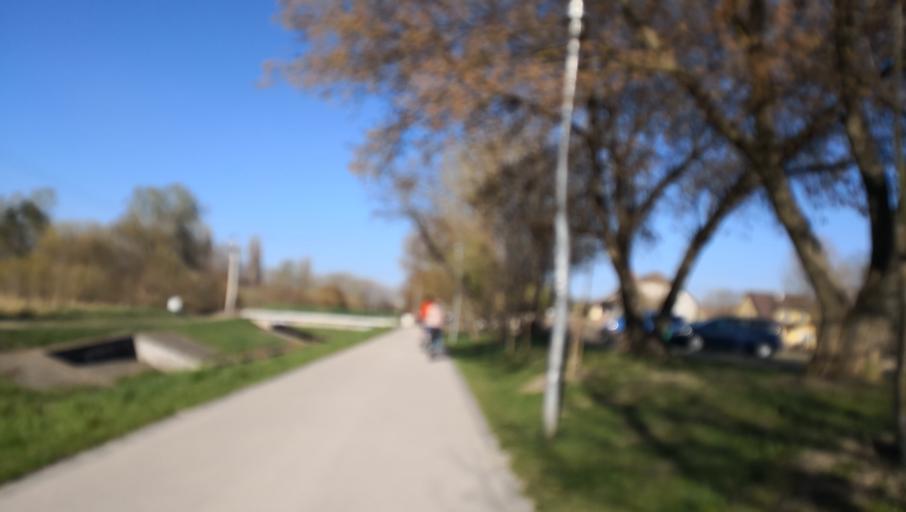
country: HU
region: Budapest
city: Budapest XVII. keruelet
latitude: 47.4894
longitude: 19.2825
